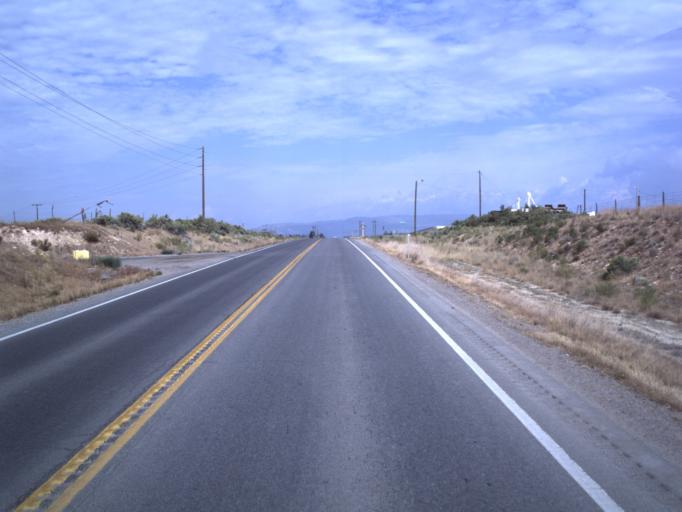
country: US
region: Utah
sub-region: Uintah County
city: Naples
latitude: 40.3953
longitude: -109.4550
